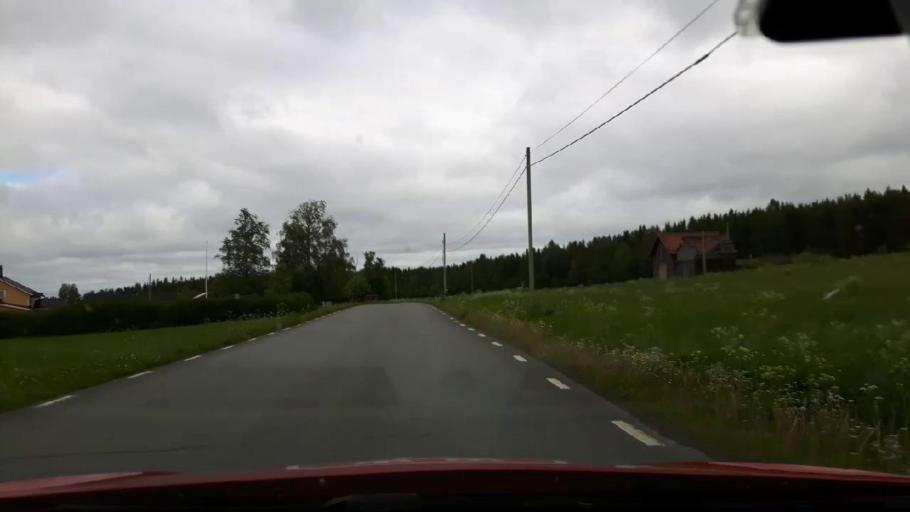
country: SE
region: Jaemtland
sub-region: Krokoms Kommun
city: Krokom
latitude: 63.2570
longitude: 14.5366
